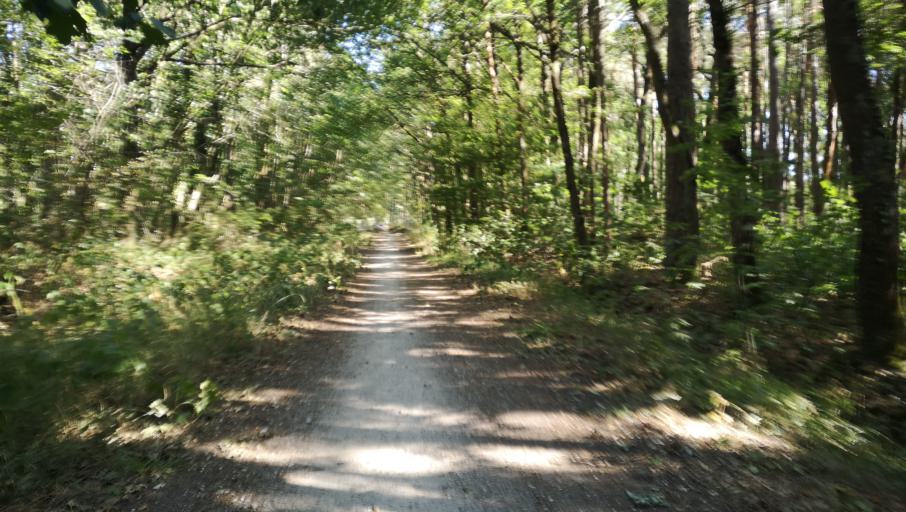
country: FR
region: Centre
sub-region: Departement du Loiret
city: Saran
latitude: 47.9614
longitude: 1.8945
